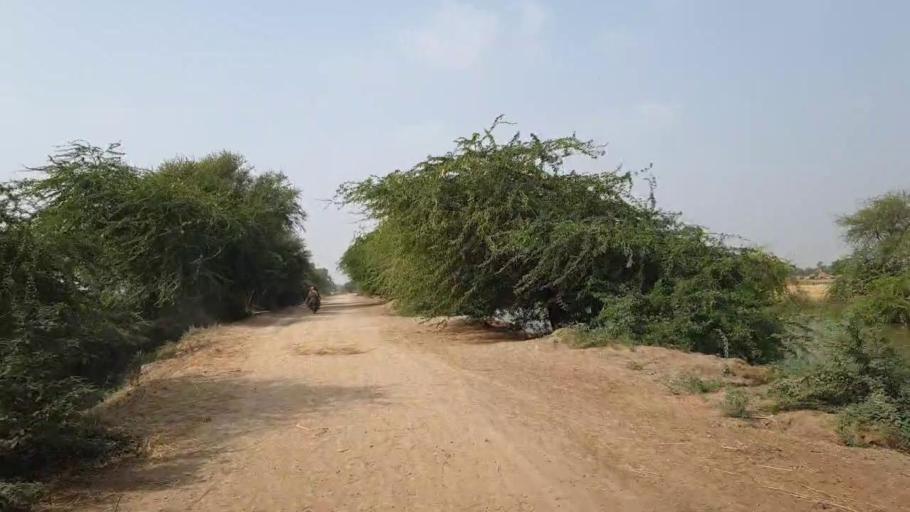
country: PK
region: Sindh
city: Kario
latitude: 24.7573
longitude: 68.5559
